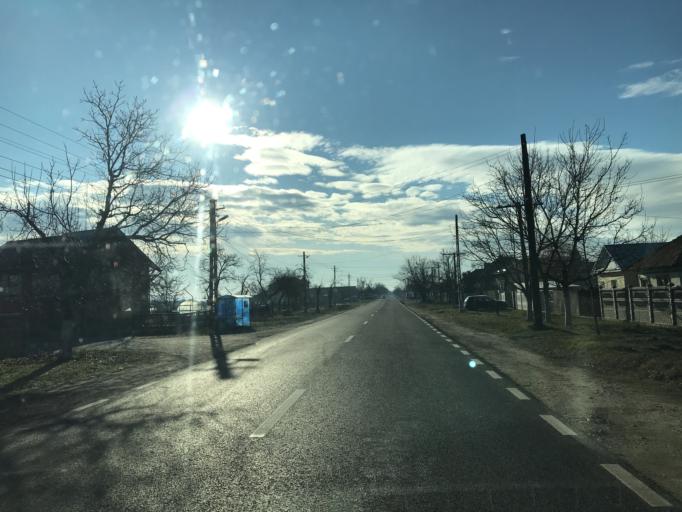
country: RO
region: Olt
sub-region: Comuna Ganeasa
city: Ganeasa
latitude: 44.3899
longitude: 24.2814
